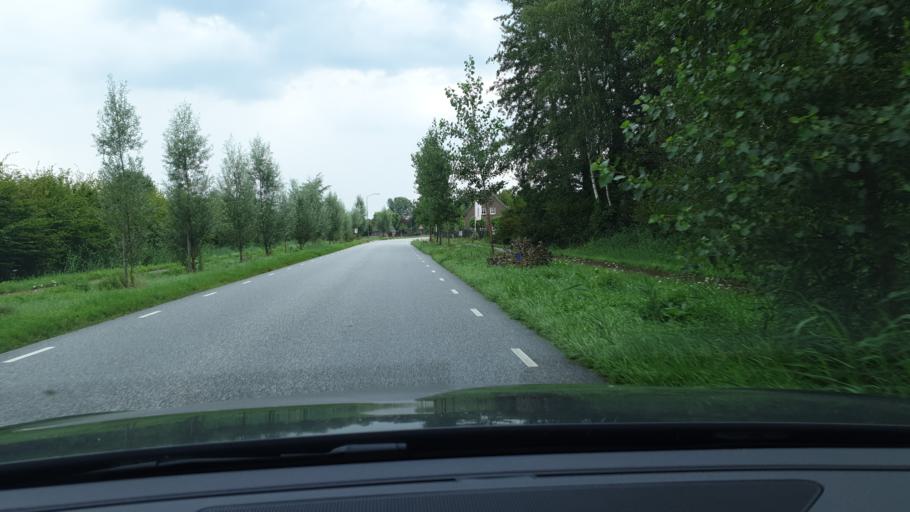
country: NL
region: North Brabant
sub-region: Gemeente Sint-Oedenrode
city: Sint-Oedenrode
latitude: 51.5531
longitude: 5.4297
